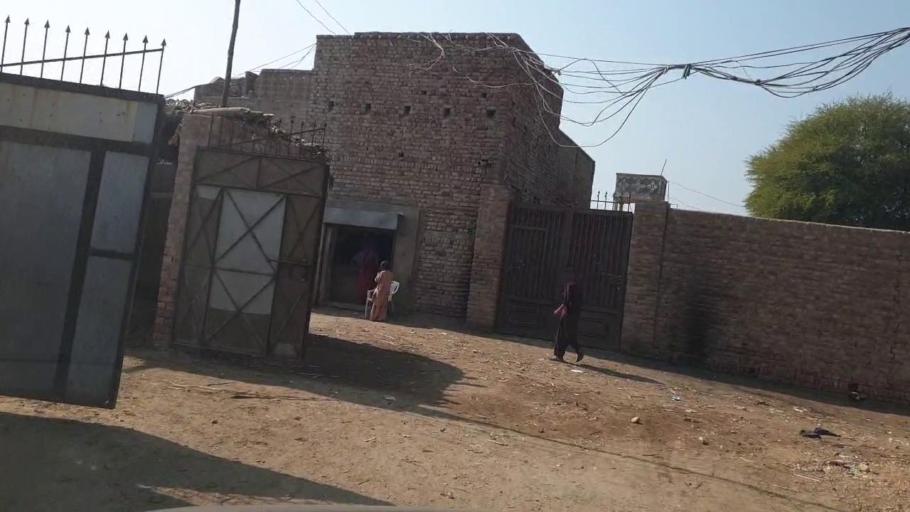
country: PK
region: Sindh
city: Bhit Shah
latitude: 25.7270
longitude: 68.5401
